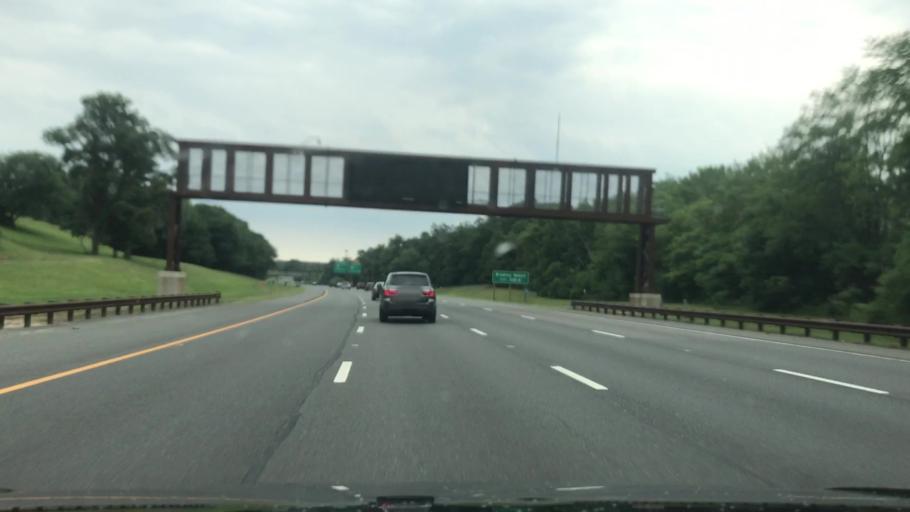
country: US
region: New Jersey
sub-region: Monmouth County
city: Shark River Hills
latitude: 40.2252
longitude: -74.0982
